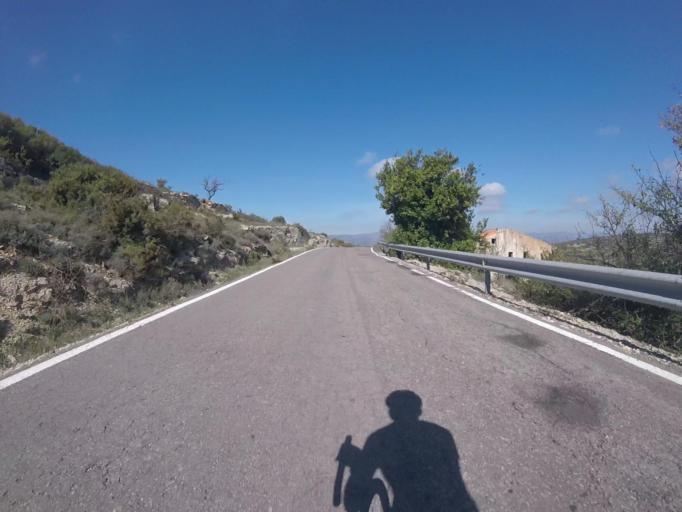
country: ES
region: Valencia
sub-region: Provincia de Castello
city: Albocasser
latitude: 40.3406
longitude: 0.0502
